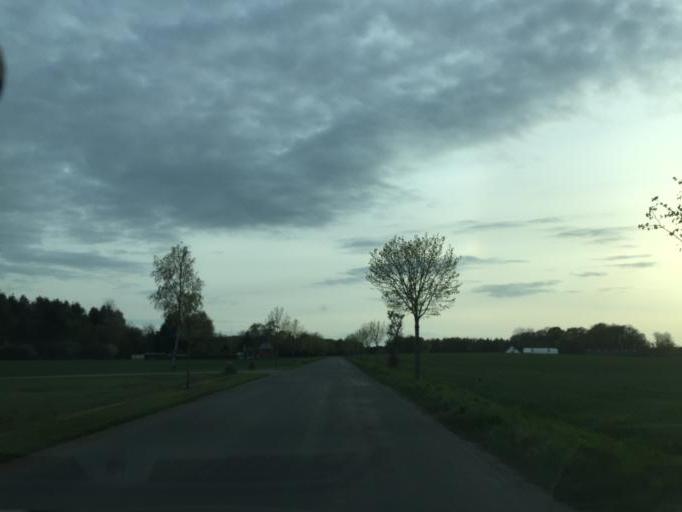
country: DK
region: South Denmark
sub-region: Faaborg-Midtfyn Kommune
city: Ringe
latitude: 55.1977
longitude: 10.5038
